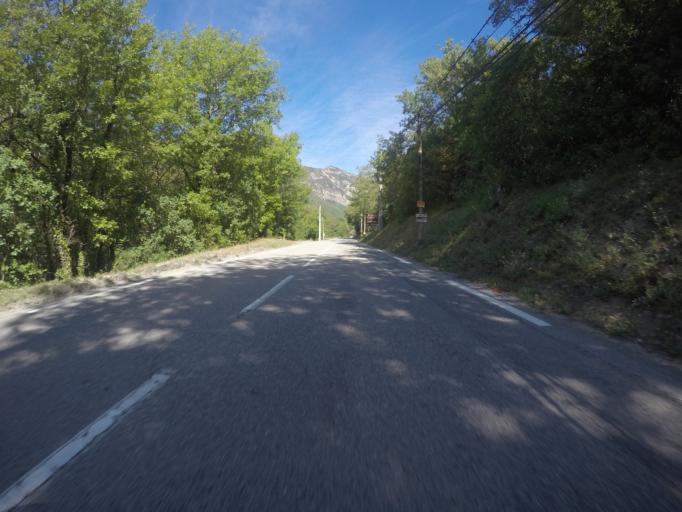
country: FR
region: Provence-Alpes-Cote d'Azur
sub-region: Departement des Alpes-Maritimes
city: Gilette
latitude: 43.9688
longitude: 7.1496
